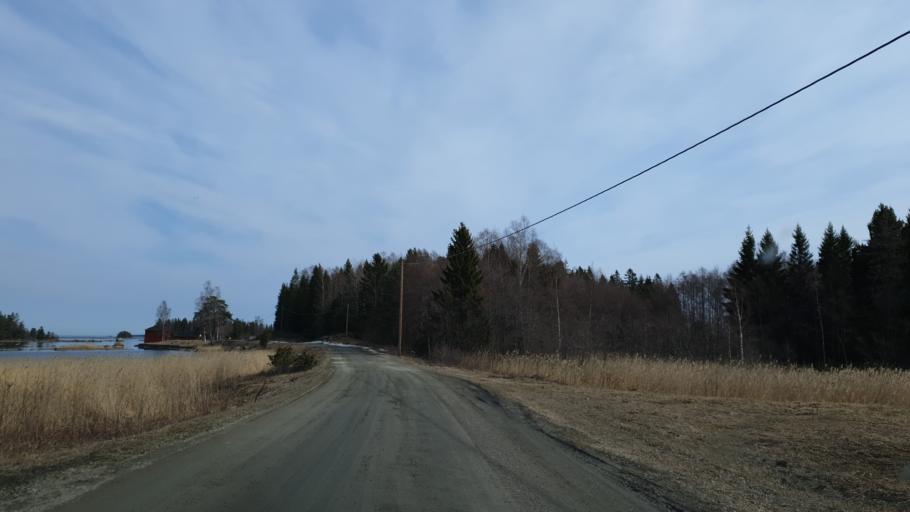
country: SE
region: Gaevleborg
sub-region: Gavle Kommun
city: Norrsundet
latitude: 61.0479
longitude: 17.1507
